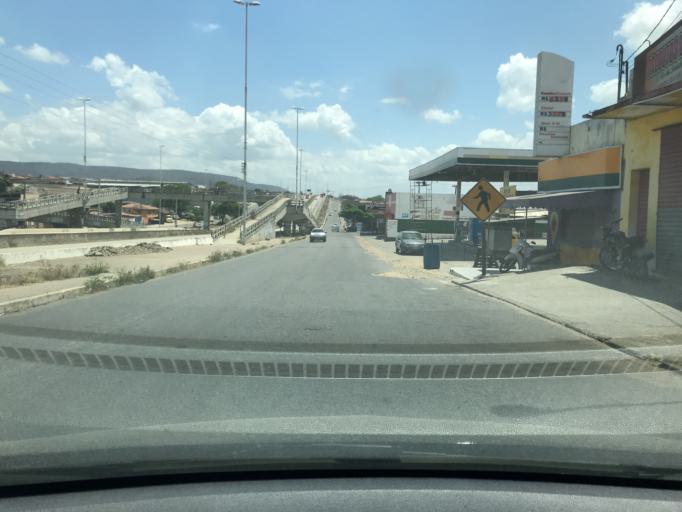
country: BR
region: Pernambuco
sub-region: Bezerros
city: Bezerros
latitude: -8.2438
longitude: -35.7539
